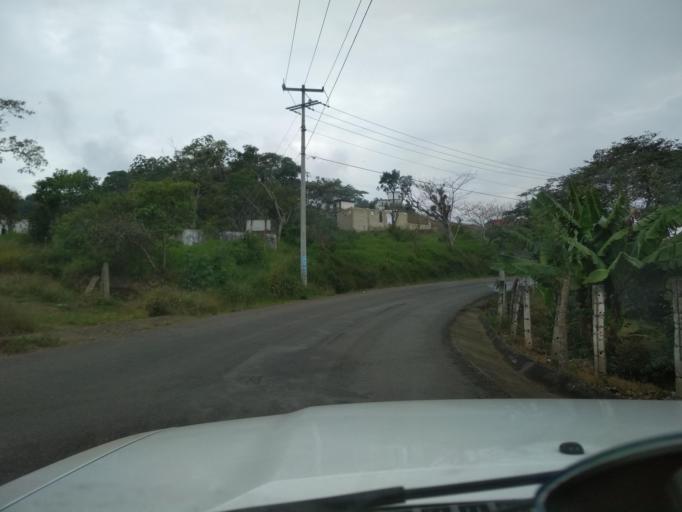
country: MX
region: Veracruz
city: El Castillo
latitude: 19.5653
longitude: -96.8679
